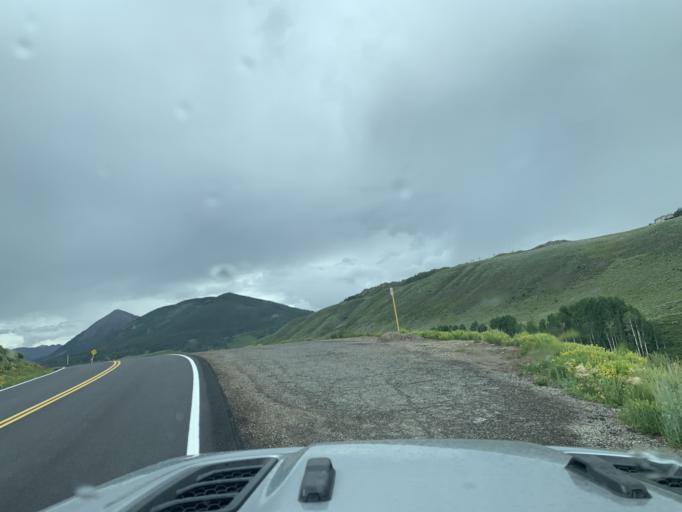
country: US
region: Colorado
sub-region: Gunnison County
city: Crested Butte
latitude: 38.8940
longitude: -106.9764
